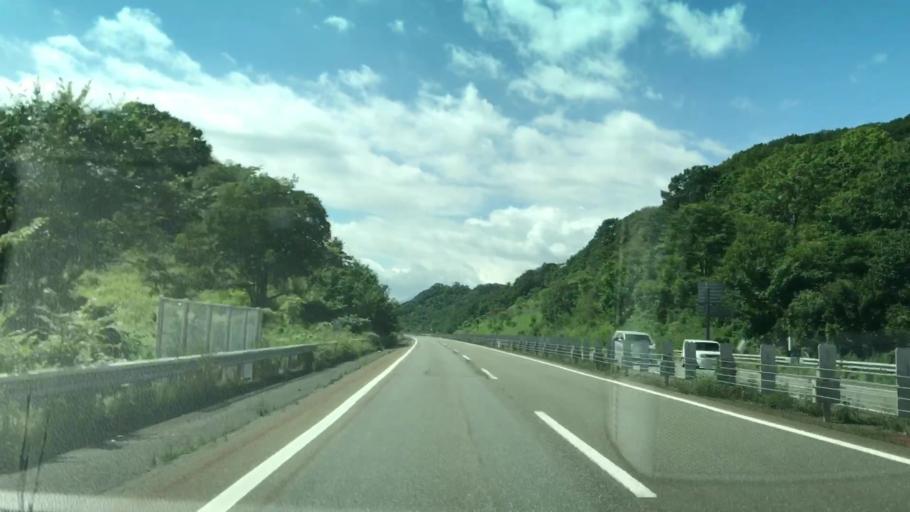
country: JP
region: Hokkaido
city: Shiraoi
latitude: 42.5625
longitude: 141.3239
